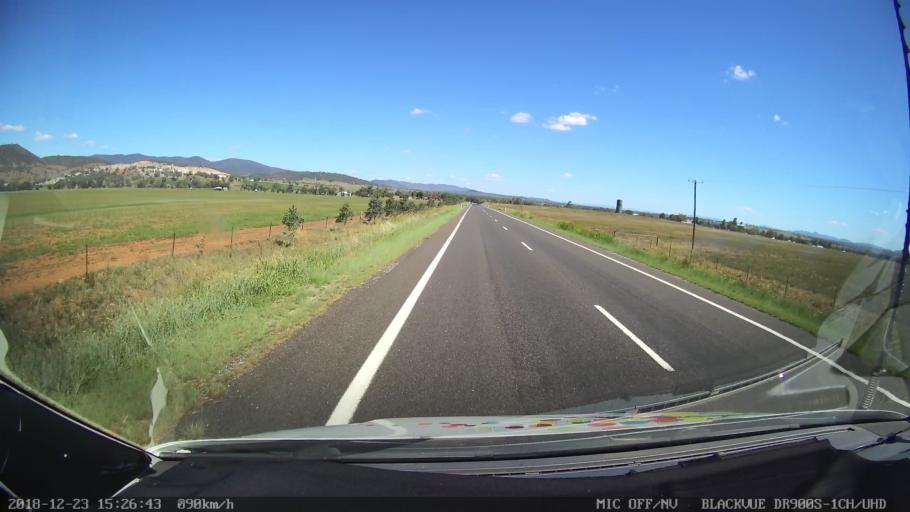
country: AU
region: New South Wales
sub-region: Tamworth Municipality
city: East Tamworth
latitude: -30.9202
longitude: 150.8405
